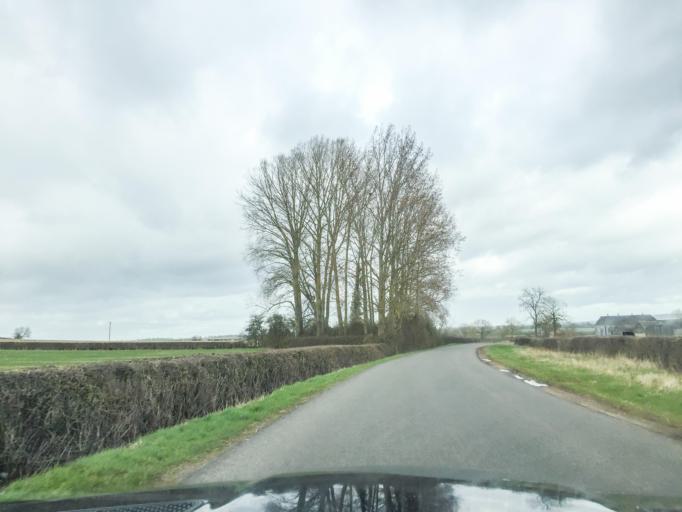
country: GB
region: England
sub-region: Warwickshire
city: Shipston on Stour
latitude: 52.0964
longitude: -1.5804
